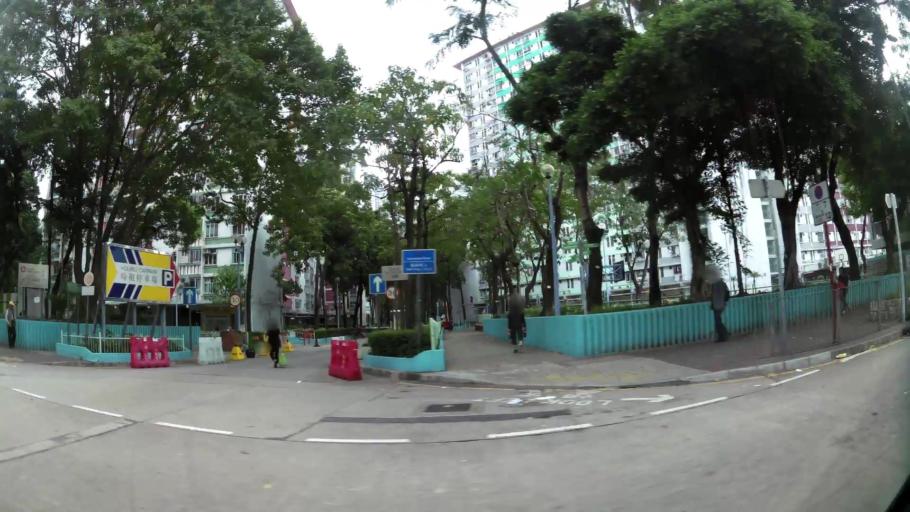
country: HK
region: Kowloon City
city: Kowloon
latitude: 22.3293
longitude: 114.2083
